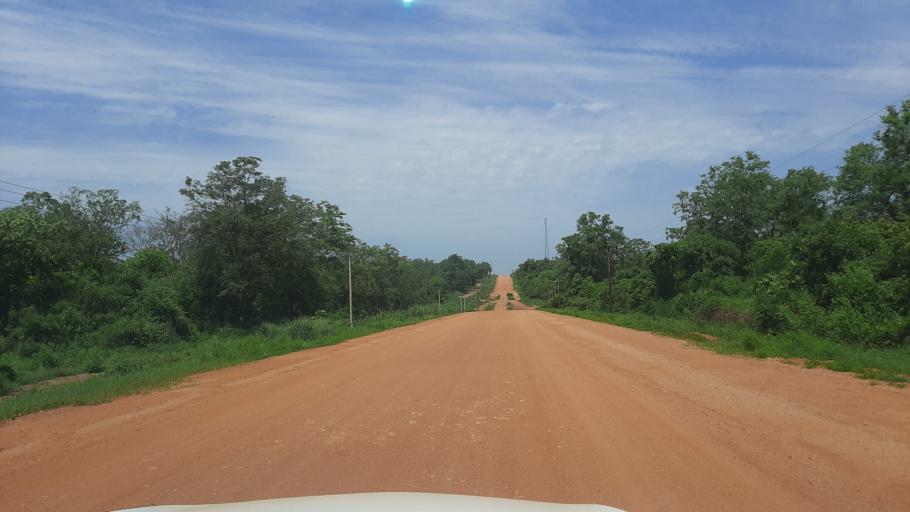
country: ET
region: Gambela
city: Gambela
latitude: 8.0692
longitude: 34.5878
